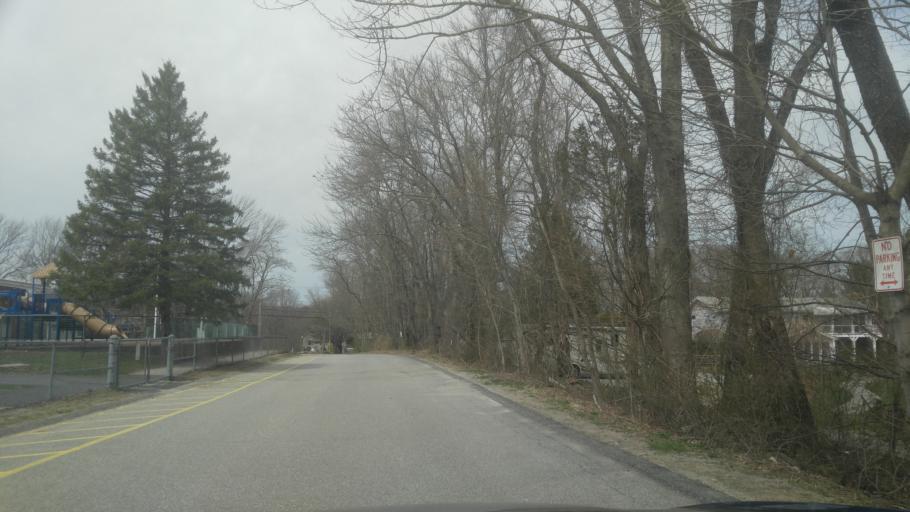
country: US
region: Rhode Island
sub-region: Washington County
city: Exeter
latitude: 41.6249
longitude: -71.5042
